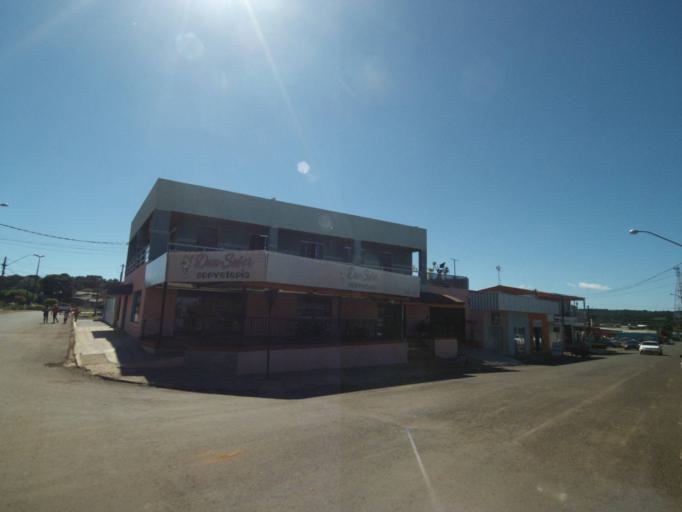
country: BR
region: Parana
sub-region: Pinhao
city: Pinhao
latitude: -25.8341
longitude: -52.0300
